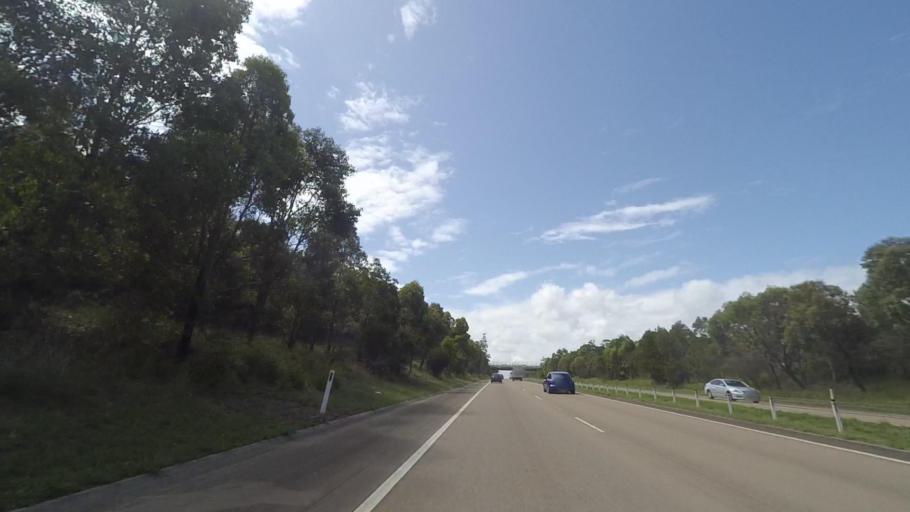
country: AU
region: New South Wales
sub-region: Lake Macquarie Shire
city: Gateshead
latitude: -32.9774
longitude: 151.6789
